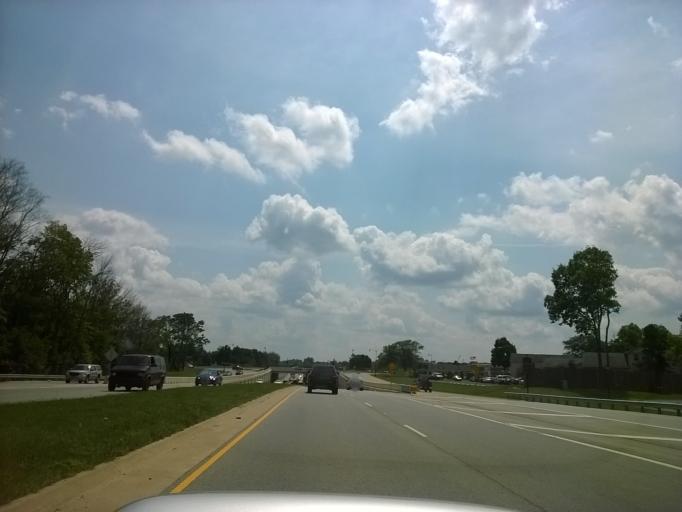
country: US
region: Indiana
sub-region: Hamilton County
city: Carmel
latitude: 39.9646
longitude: -86.1134
